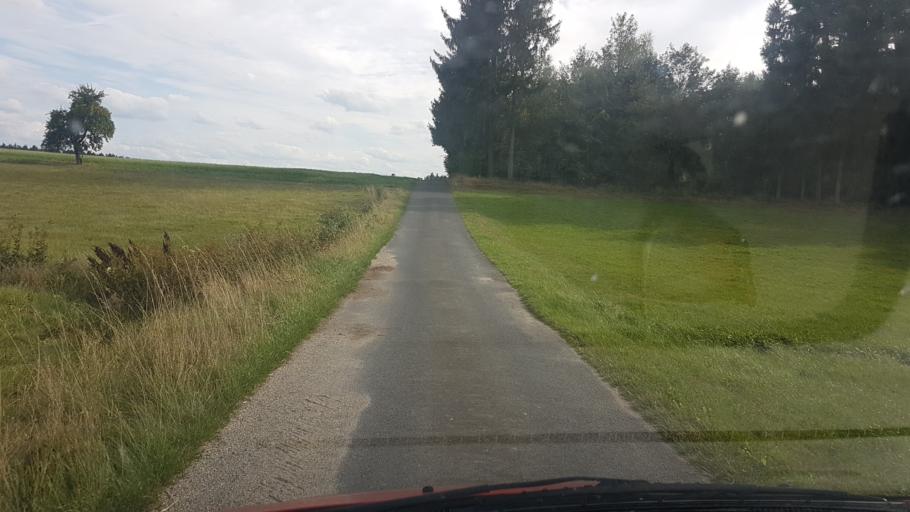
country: DE
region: Bavaria
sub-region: Upper Franconia
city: Hochstadt bei Thiersheim
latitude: 50.0746
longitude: 12.0682
